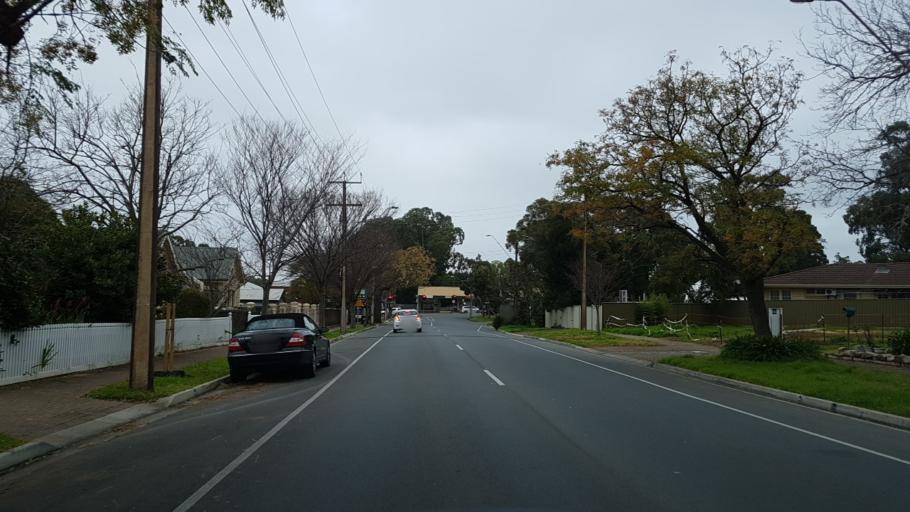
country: AU
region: South Australia
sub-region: Burnside
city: Tusmore
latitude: -34.9402
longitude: 138.6514
